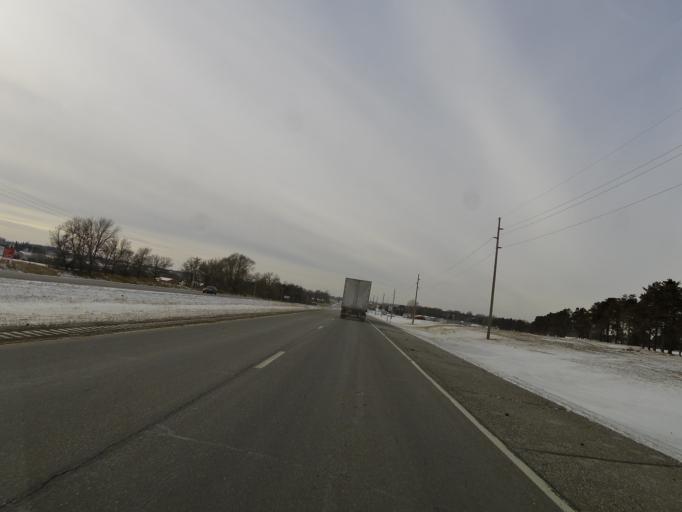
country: US
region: Minnesota
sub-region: Scott County
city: Belle Plaine
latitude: 44.6305
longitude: -93.7349
